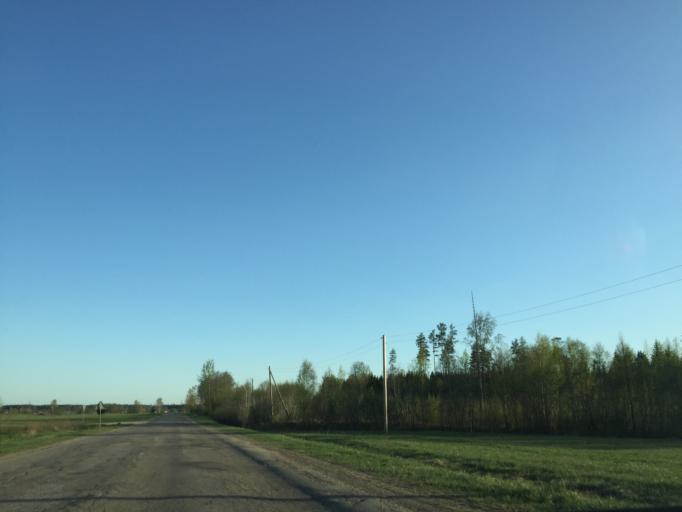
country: LV
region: Koknese
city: Koknese
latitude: 56.6921
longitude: 25.4870
